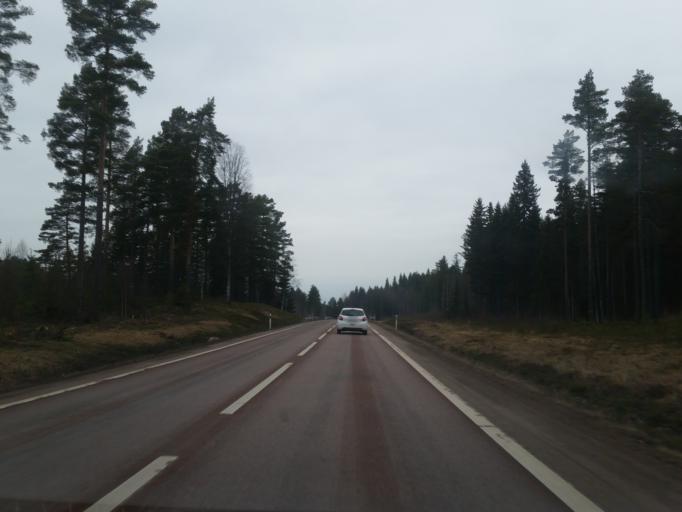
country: SE
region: Dalarna
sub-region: Alvdalens Kommun
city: AElvdalen
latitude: 61.2044
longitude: 14.0683
